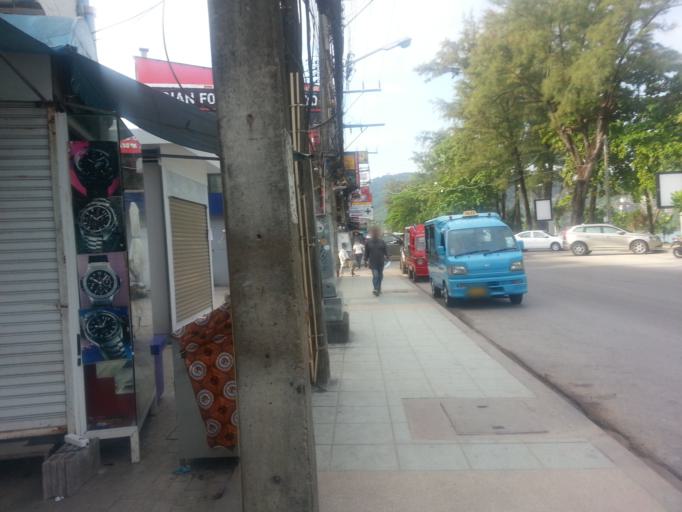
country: TH
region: Phuket
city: Patong
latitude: 7.8920
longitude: 98.2943
